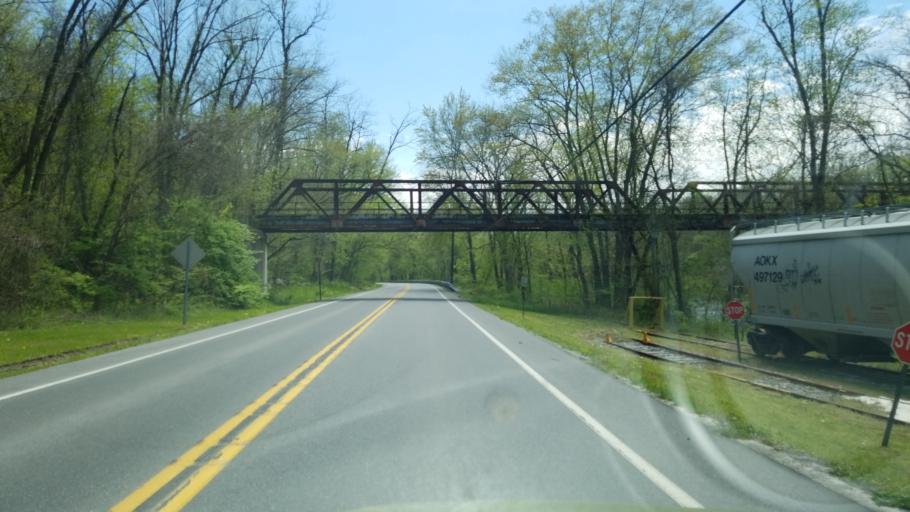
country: US
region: Pennsylvania
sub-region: Huntingdon County
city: Mount Union
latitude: 40.4052
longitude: -77.9376
